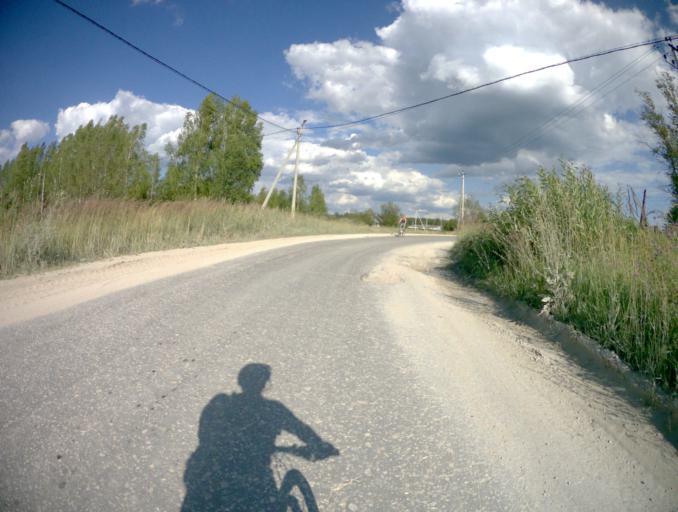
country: RU
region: Vladimir
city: Krasnyy Bogatyr'
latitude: 55.9822
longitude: 41.1198
